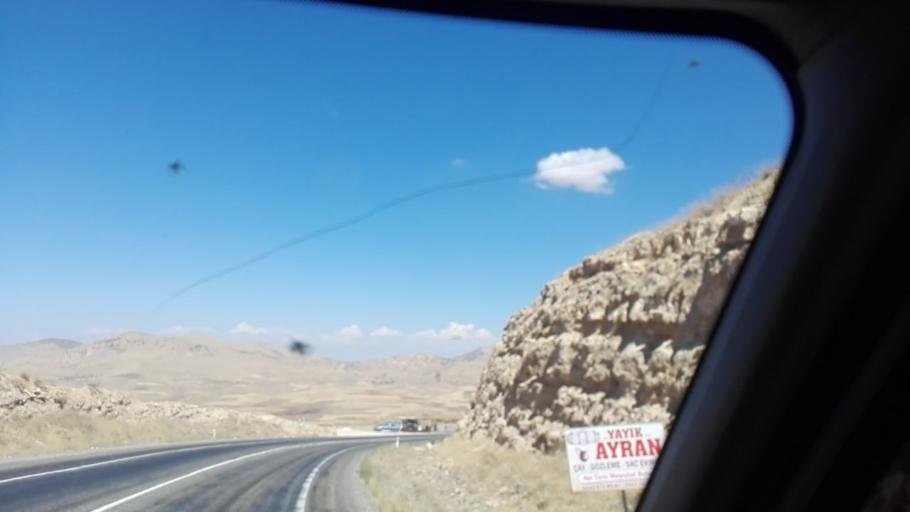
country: TR
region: Batman
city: Gerdzhyush
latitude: 37.5602
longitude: 41.3608
